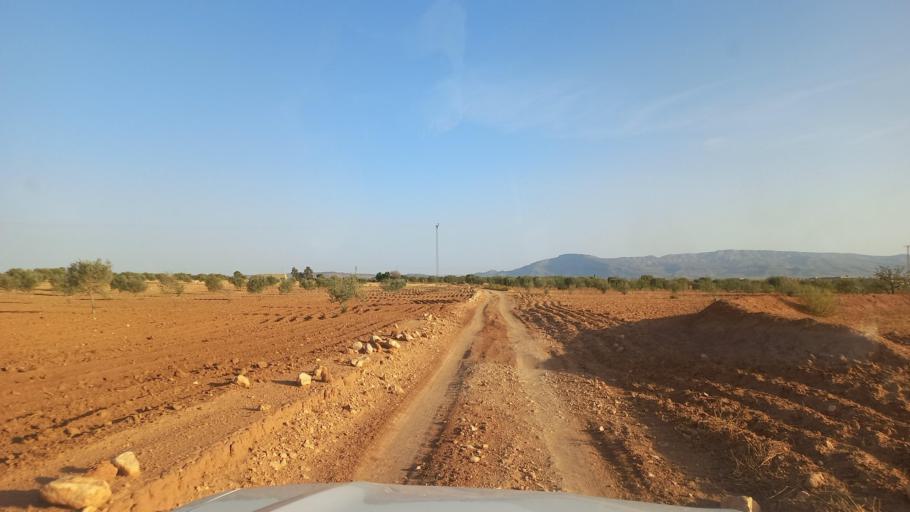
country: TN
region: Al Qasrayn
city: Kasserine
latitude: 35.2586
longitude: 8.9065
